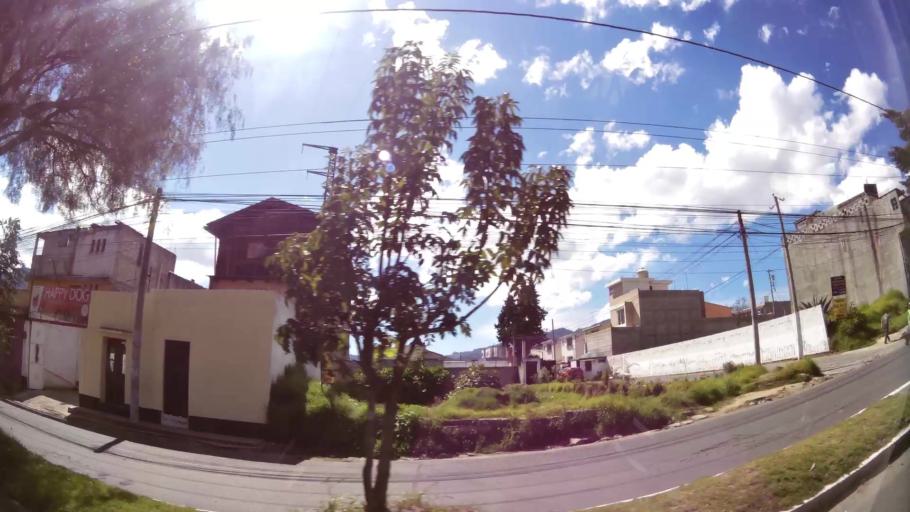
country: GT
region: Quetzaltenango
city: Quetzaltenango
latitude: 14.8433
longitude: -91.5298
